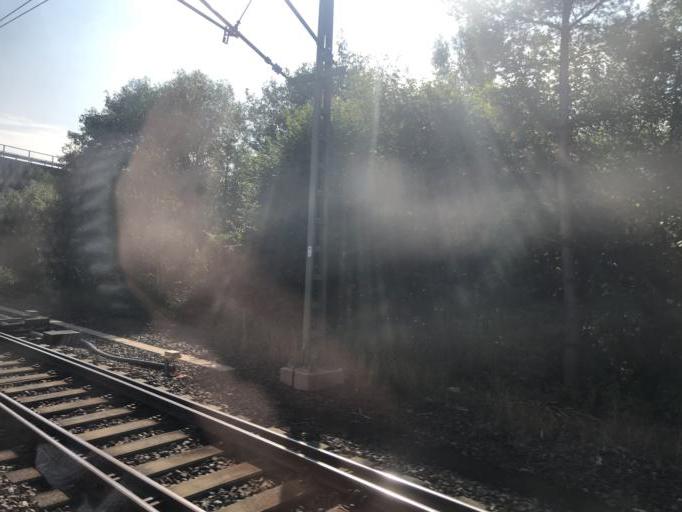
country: DE
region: Rheinland-Pfalz
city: Ellweiler
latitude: 49.6025
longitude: 7.1658
